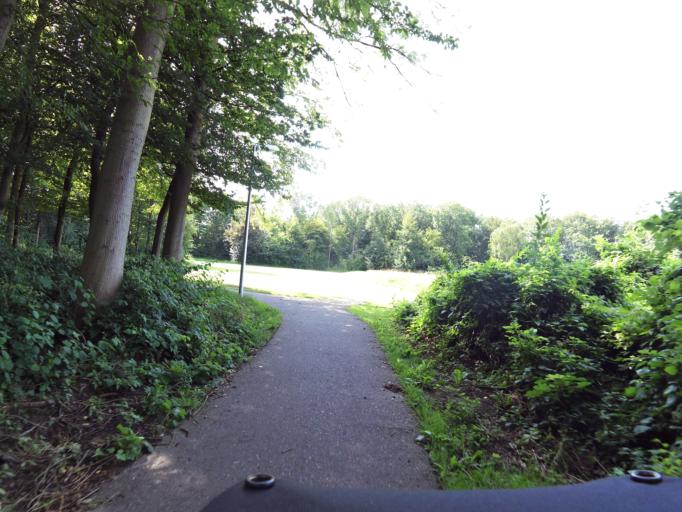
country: NL
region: South Holland
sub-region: Gemeente Goeree-Overflakkee
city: Middelharnis
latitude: 51.7612
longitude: 4.1730
